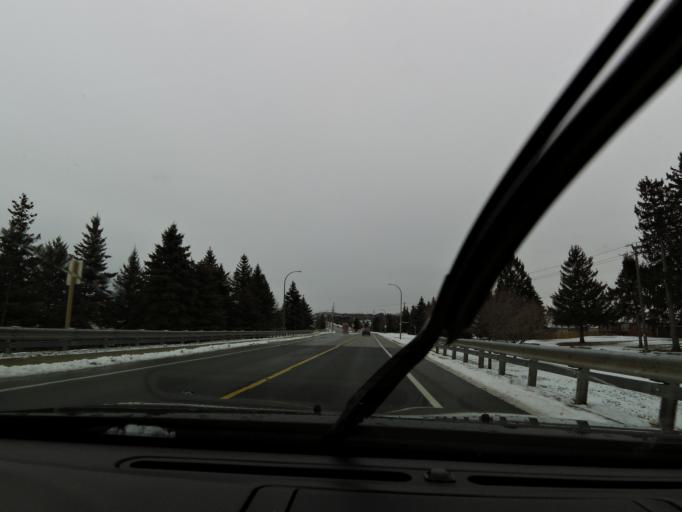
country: CA
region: Ontario
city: Ancaster
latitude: 43.2254
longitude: -79.9563
